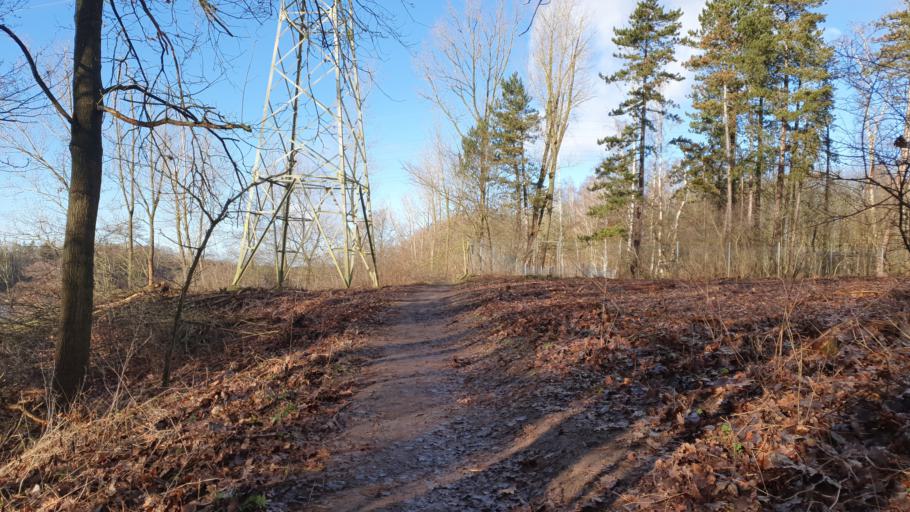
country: DE
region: Mecklenburg-Vorpommern
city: Neumuehle
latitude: 53.6357
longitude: 11.3503
